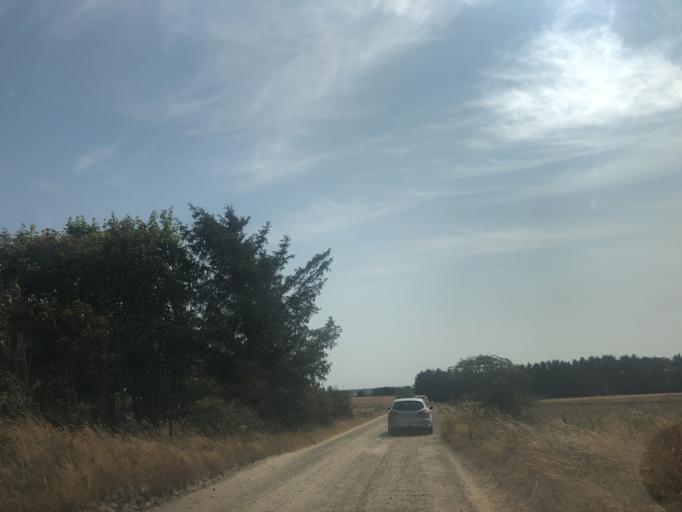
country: DK
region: North Denmark
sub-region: Morso Kommune
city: Nykobing Mors
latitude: 56.8242
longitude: 8.9816
